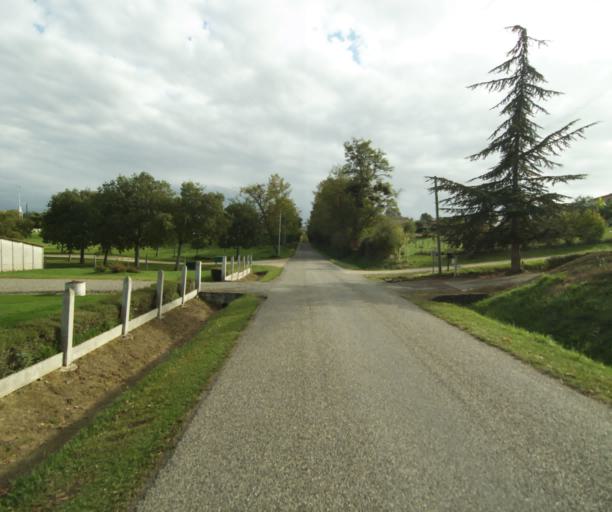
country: FR
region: Midi-Pyrenees
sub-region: Departement du Gers
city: Eauze
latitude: 43.8678
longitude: 0.1010
